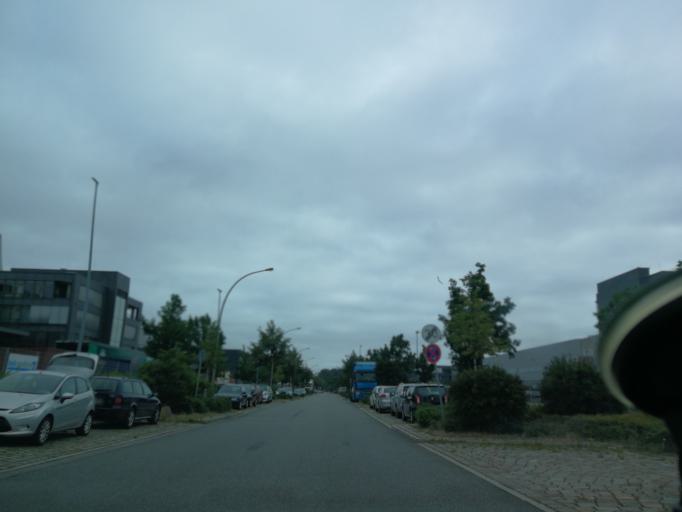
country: DE
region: Hamburg
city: Altona
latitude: 53.5043
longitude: 9.9260
